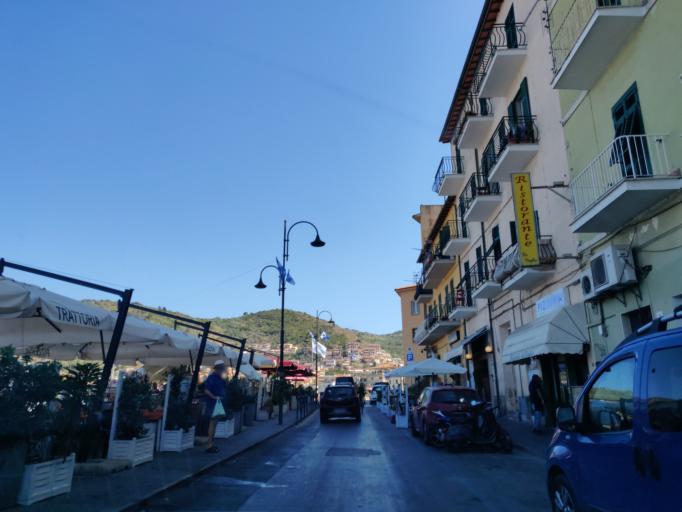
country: IT
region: Tuscany
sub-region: Provincia di Grosseto
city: Monte Argentario
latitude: 42.4367
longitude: 11.1201
